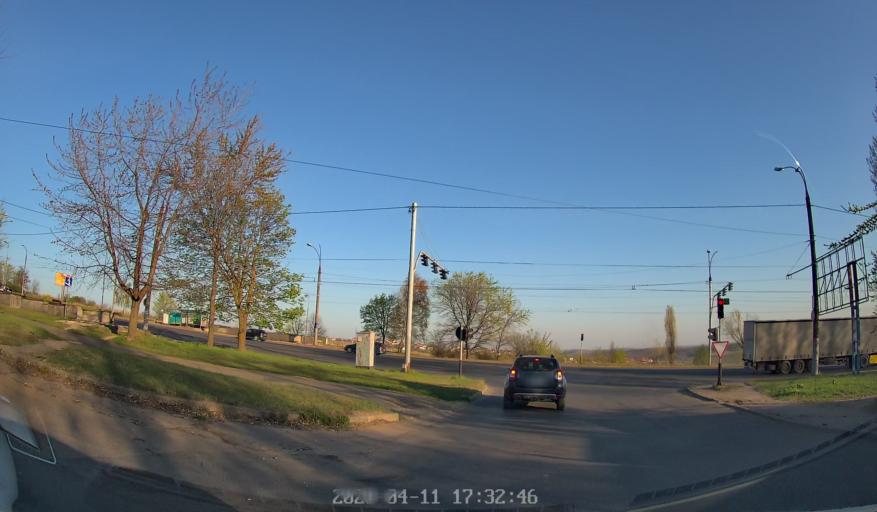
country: MD
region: Laloveni
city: Ialoveni
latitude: 46.9919
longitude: 28.7886
